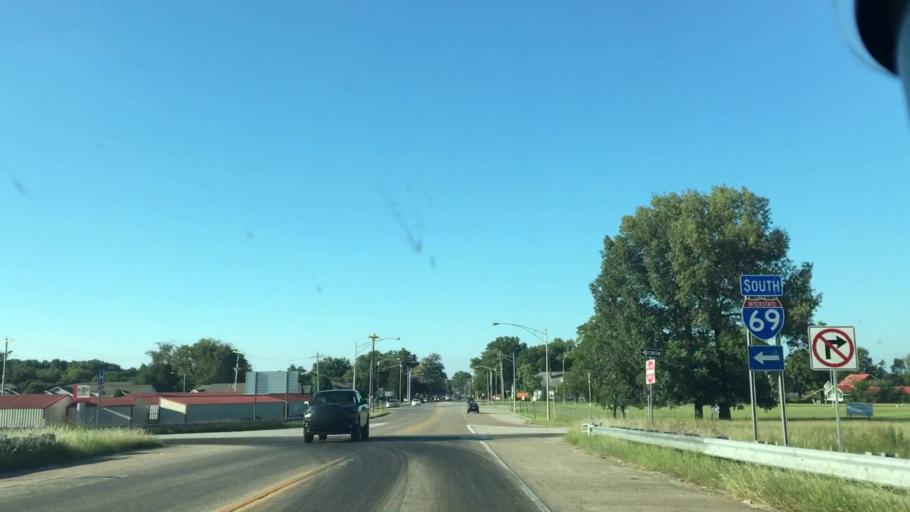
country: US
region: Indiana
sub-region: Vanderburgh County
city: Evansville
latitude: 37.9400
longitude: -87.4927
